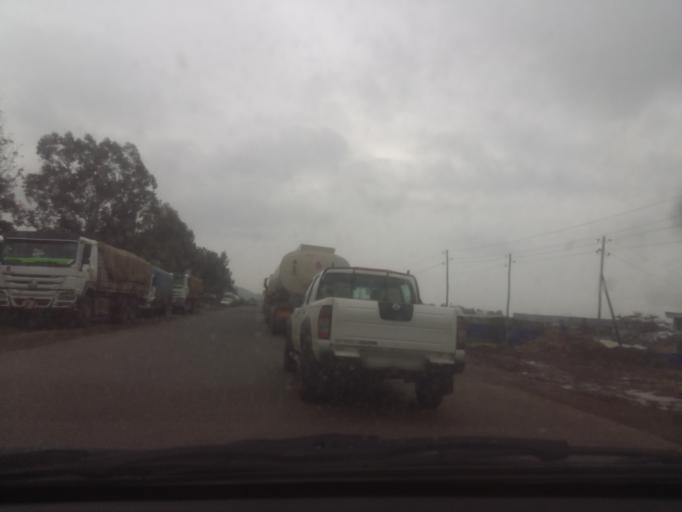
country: ET
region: Oromiya
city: Bishoftu
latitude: 8.8188
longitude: 38.8736
